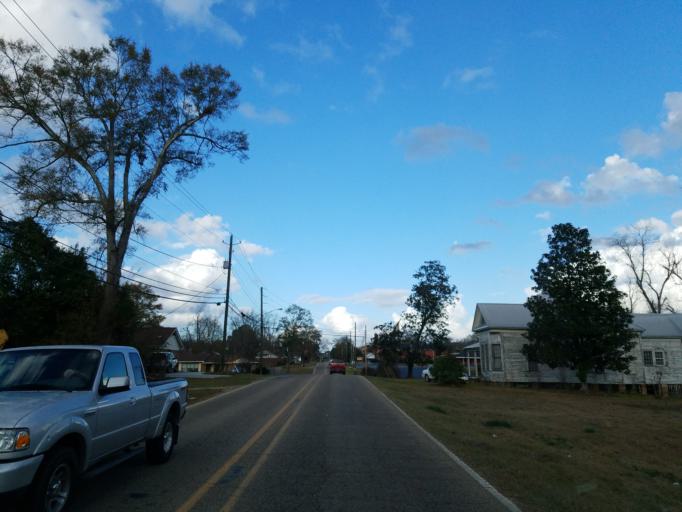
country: US
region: Mississippi
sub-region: Jones County
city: Ellisville
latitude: 31.6002
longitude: -89.1962
